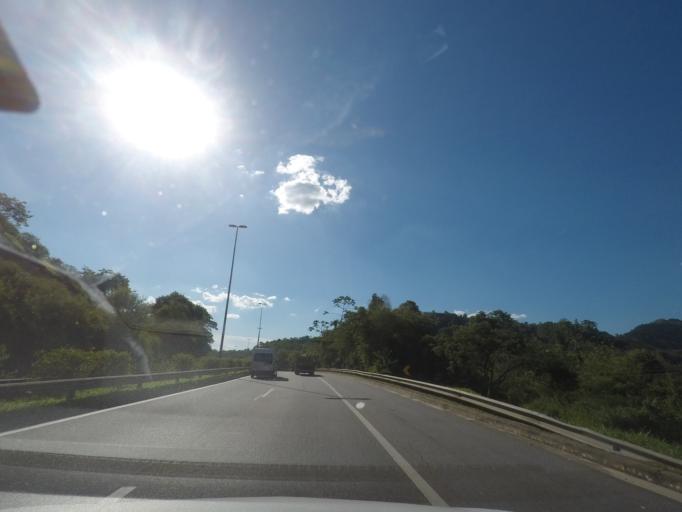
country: BR
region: Rio de Janeiro
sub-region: Petropolis
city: Petropolis
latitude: -22.6561
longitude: -43.1219
